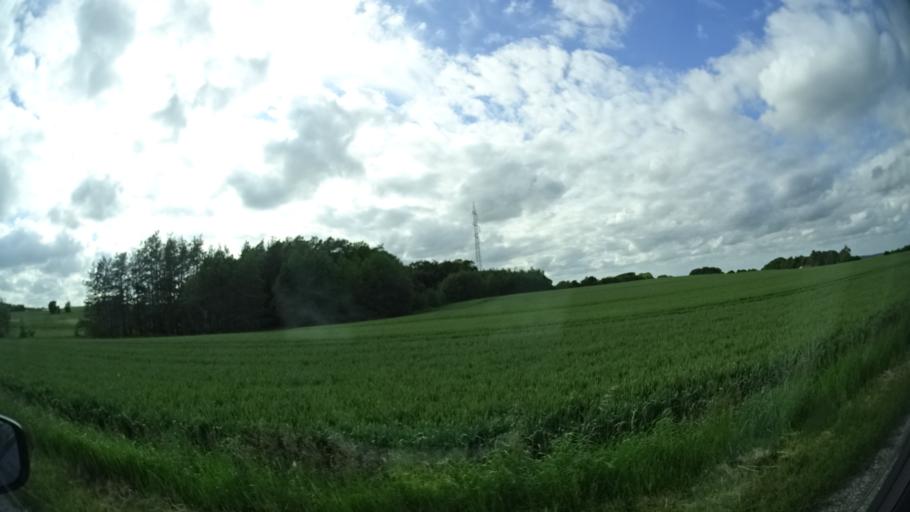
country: DK
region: Central Jutland
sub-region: Syddjurs Kommune
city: Ronde
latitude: 56.3220
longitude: 10.4325
